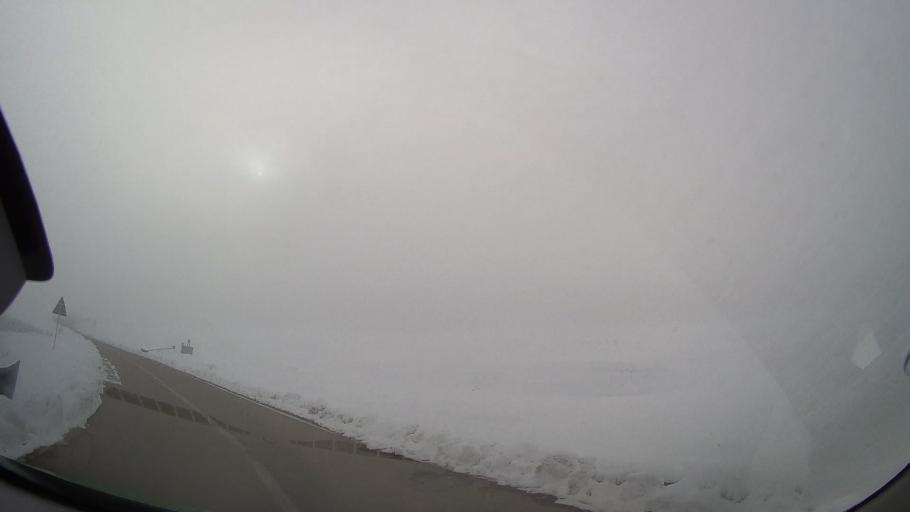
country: RO
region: Iasi
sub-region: Comuna Valea Seaca
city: Topile
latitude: 47.2705
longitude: 26.6694
